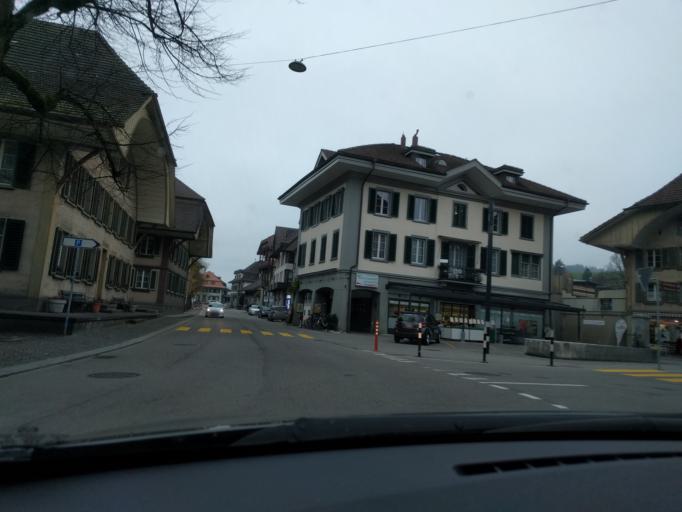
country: CH
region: Bern
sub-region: Emmental District
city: Langnau
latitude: 46.9401
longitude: 7.7859
